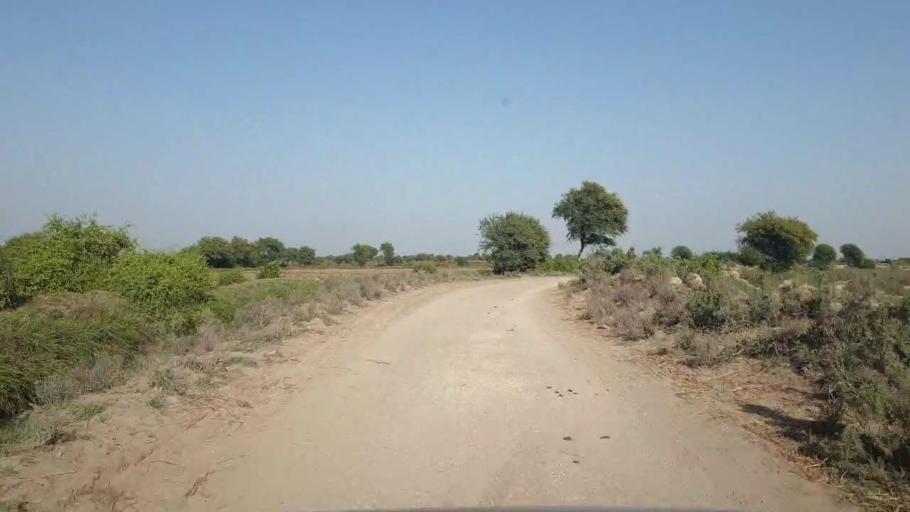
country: PK
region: Sindh
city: Rajo Khanani
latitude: 25.0093
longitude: 68.7821
